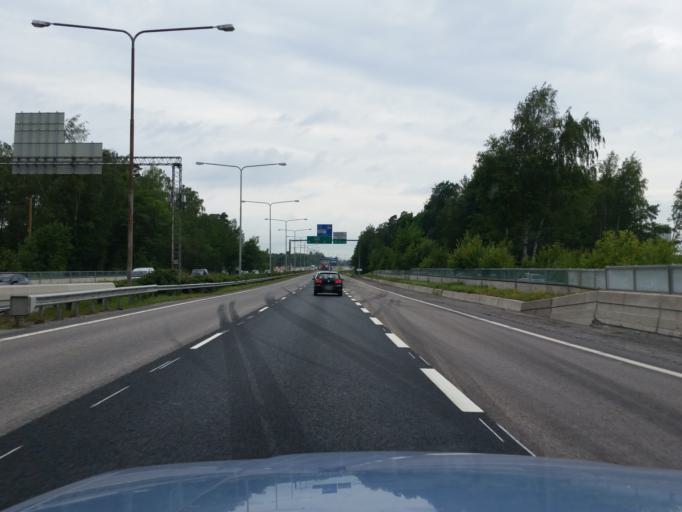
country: FI
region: Uusimaa
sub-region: Helsinki
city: Teekkarikylae
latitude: 60.1642
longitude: 24.8535
